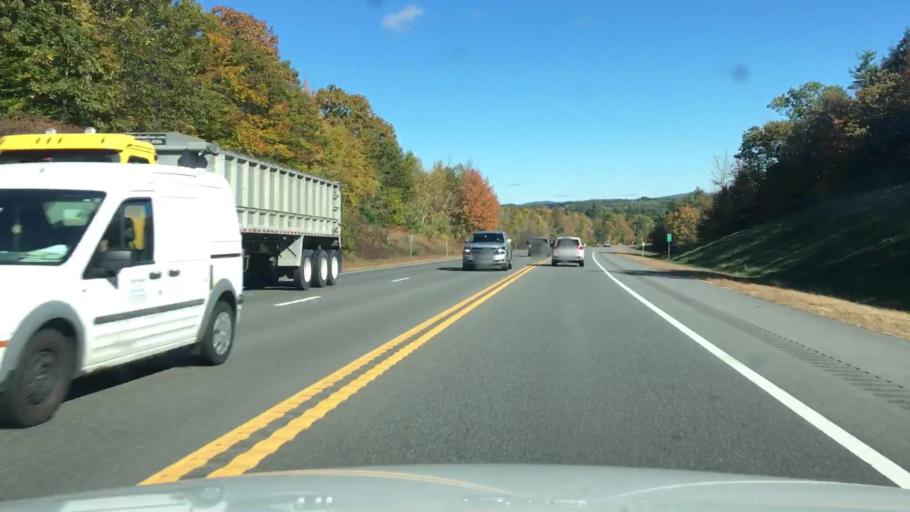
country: US
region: New Hampshire
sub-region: Strafford County
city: Farmington
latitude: 43.4408
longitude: -71.0052
